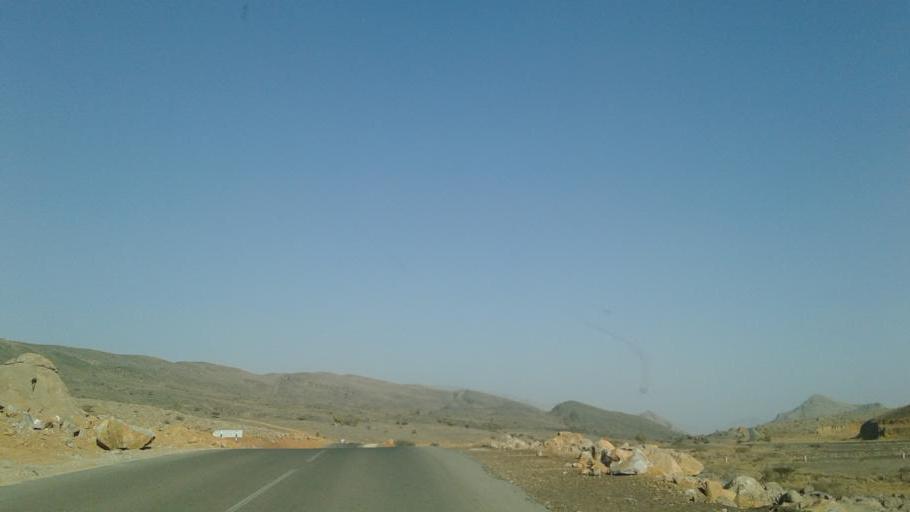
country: OM
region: Muhafazat ad Dakhiliyah
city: Bahla'
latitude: 23.0780
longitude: 57.3505
